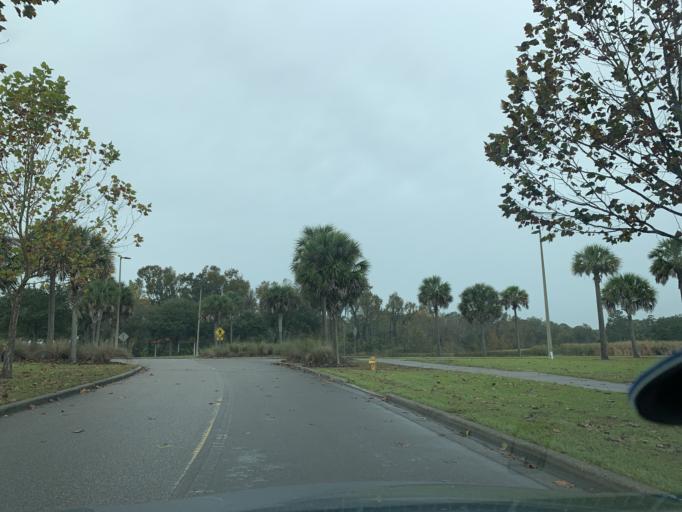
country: US
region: Florida
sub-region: Pasco County
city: Wesley Chapel
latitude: 28.2707
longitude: -82.3226
